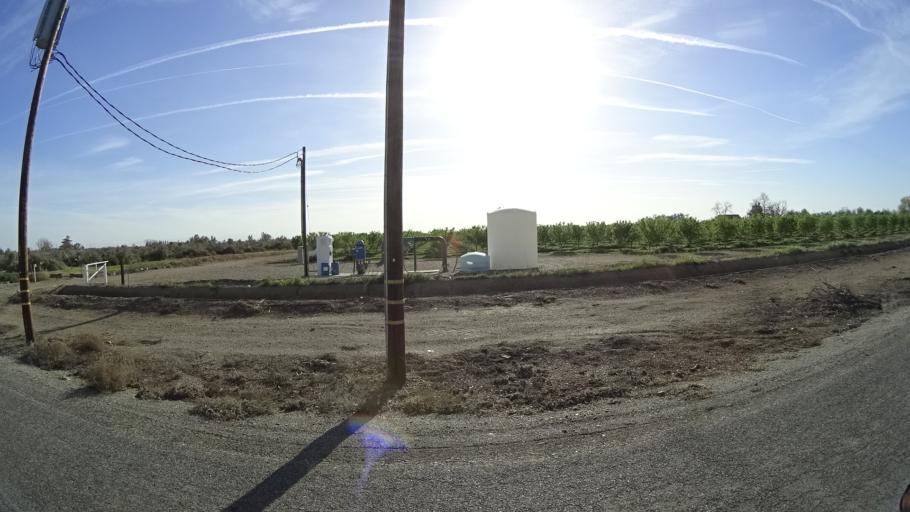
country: US
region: California
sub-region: Glenn County
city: Orland
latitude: 39.7222
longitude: -122.2347
